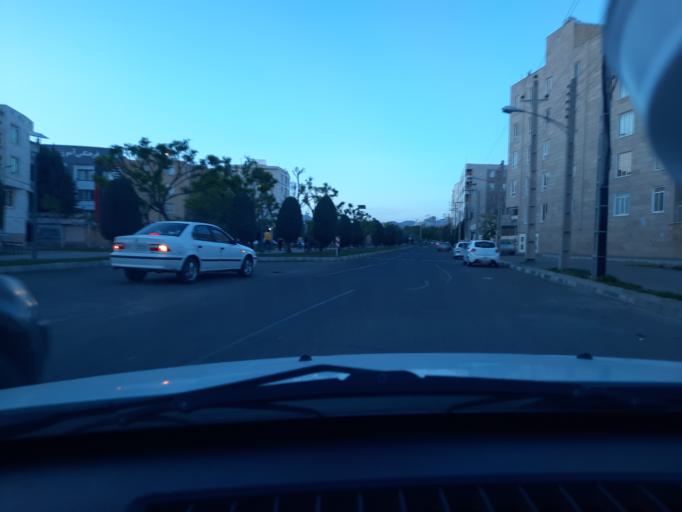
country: IR
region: Qazvin
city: Qazvin
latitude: 36.2993
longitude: 50.0120
